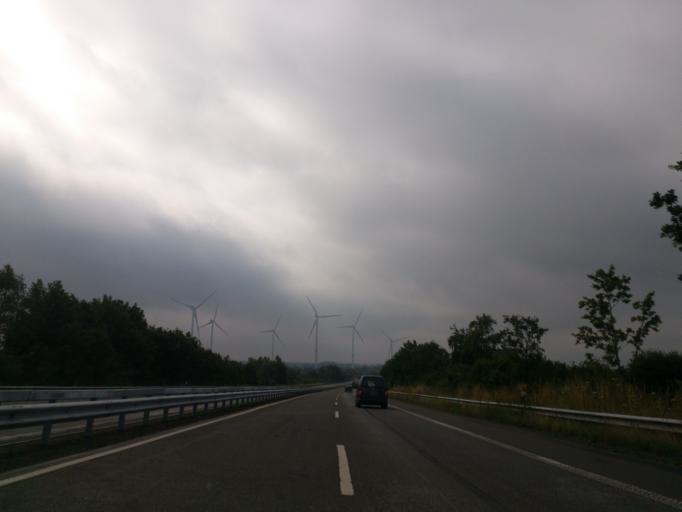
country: DE
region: Schleswig-Holstein
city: Arkebek
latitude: 54.1496
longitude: 9.2398
